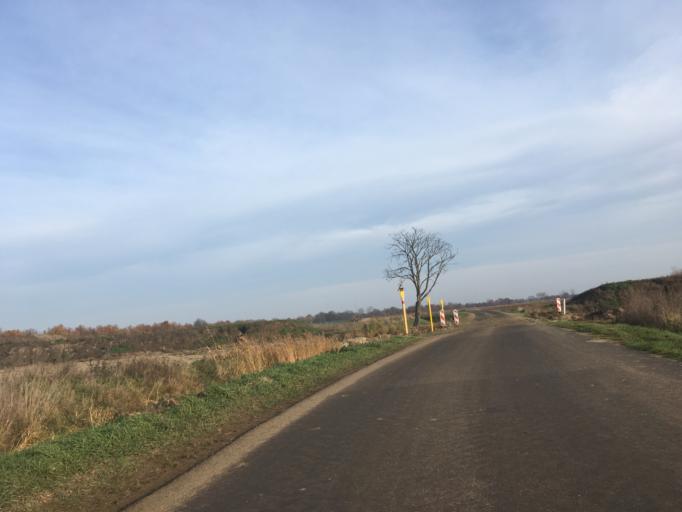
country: DE
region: Brandenburg
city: Bad Freienwalde
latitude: 52.7706
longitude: 14.0921
